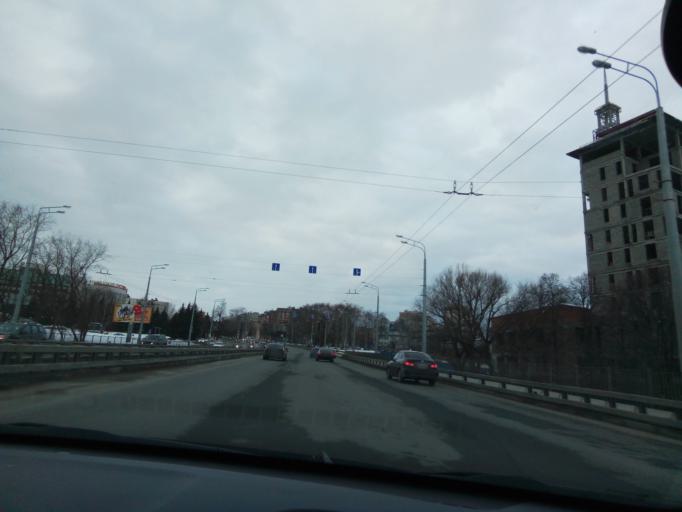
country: RU
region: Chuvashia
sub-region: Cheboksarskiy Rayon
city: Cheboksary
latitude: 56.1454
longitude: 47.2405
